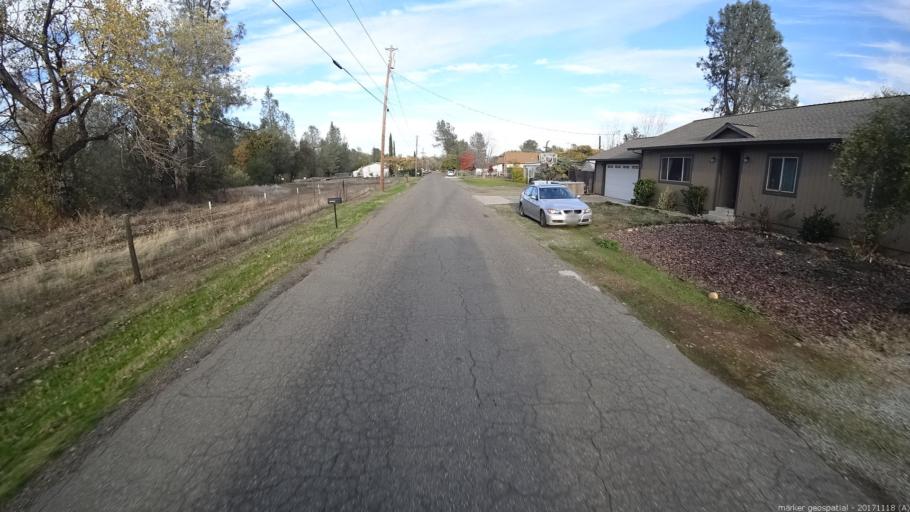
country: US
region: California
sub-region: Shasta County
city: Anderson
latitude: 40.4614
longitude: -122.3337
